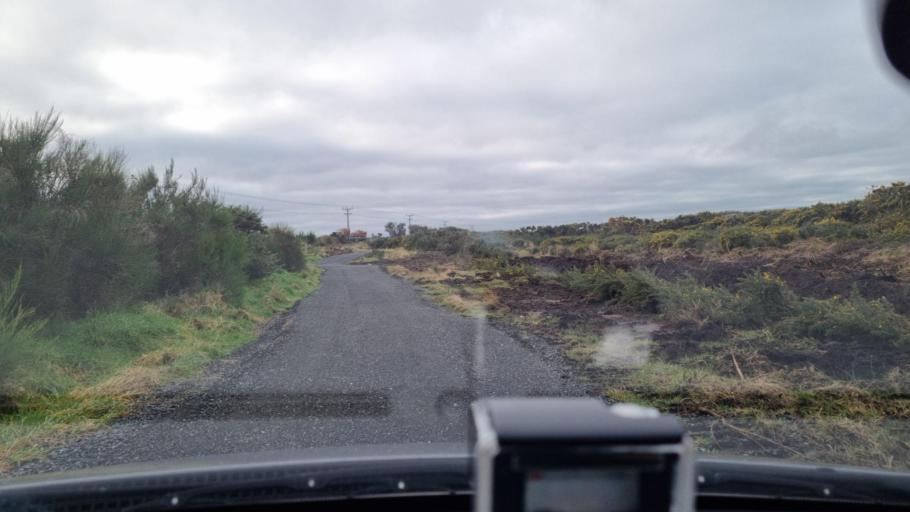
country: NZ
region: Southland
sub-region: Invercargill City
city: Bluff
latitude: -46.5395
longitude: 168.3031
